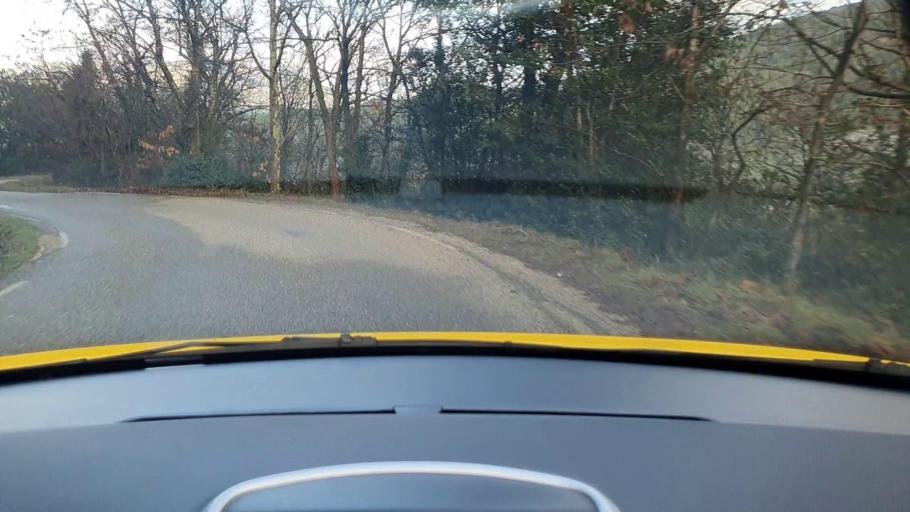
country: FR
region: Languedoc-Roussillon
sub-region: Departement du Gard
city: Branoux-les-Taillades
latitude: 44.2995
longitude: 3.9937
